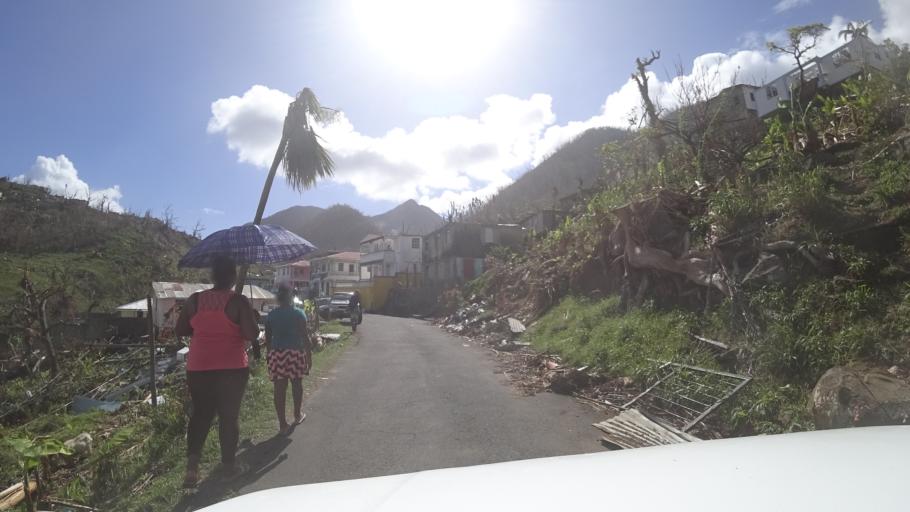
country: DM
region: Saint Patrick
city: Berekua
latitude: 15.2403
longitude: -61.3221
